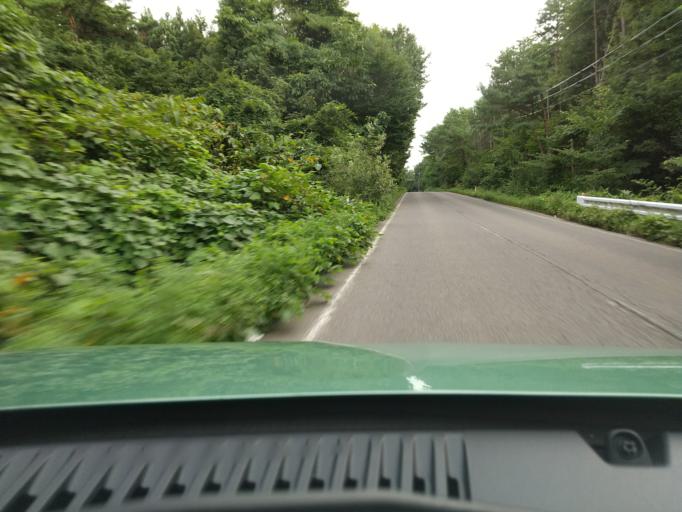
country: JP
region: Akita
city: Akita
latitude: 39.7675
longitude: 140.1343
